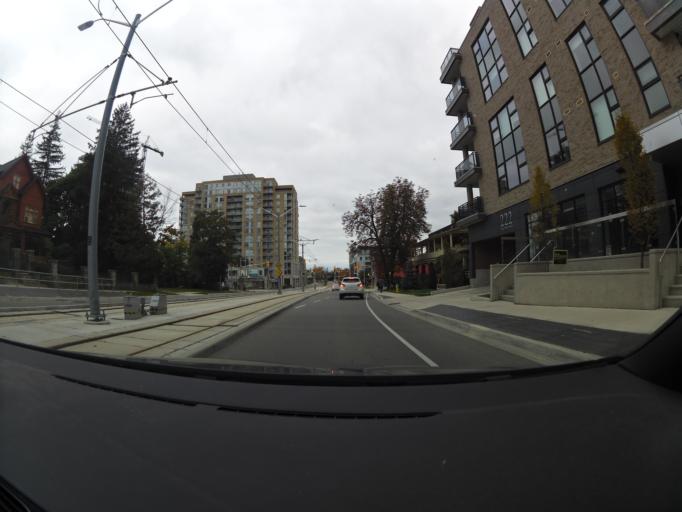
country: CA
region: Ontario
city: Waterloo
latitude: 43.4591
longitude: -80.5166
